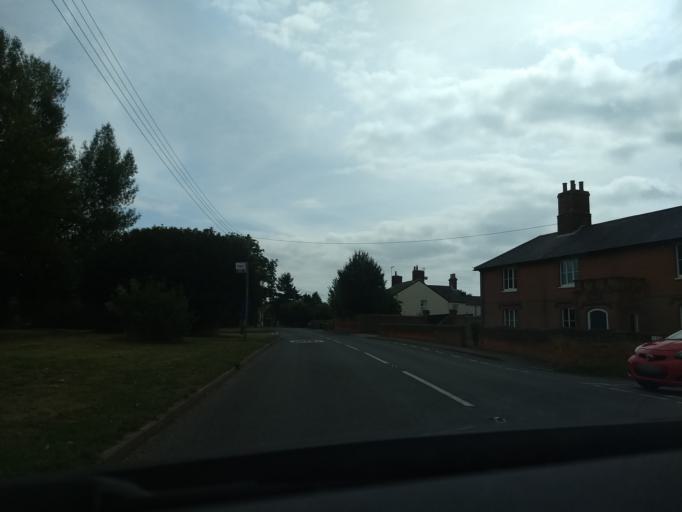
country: GB
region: England
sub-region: Suffolk
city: Shotley Gate
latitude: 51.9897
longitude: 1.2046
